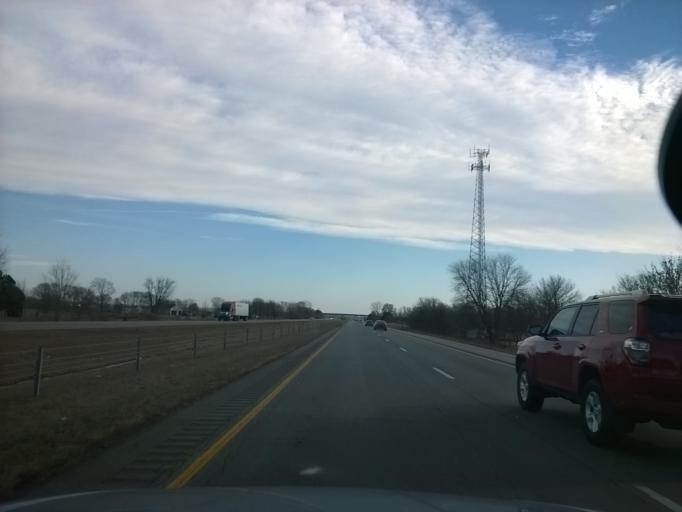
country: US
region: Indiana
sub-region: Johnson County
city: Edinburgh
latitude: 39.4249
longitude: -85.9718
